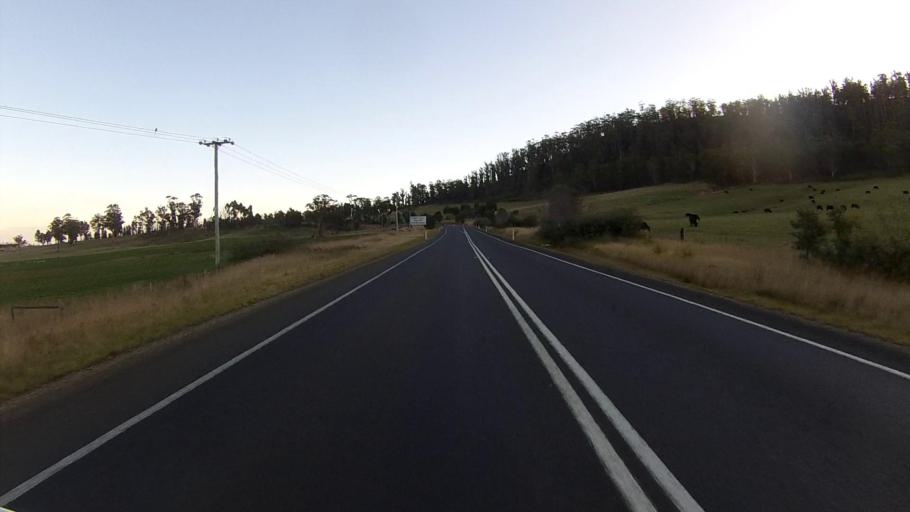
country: AU
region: Tasmania
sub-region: Sorell
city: Sorell
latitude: -42.8199
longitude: 147.7454
